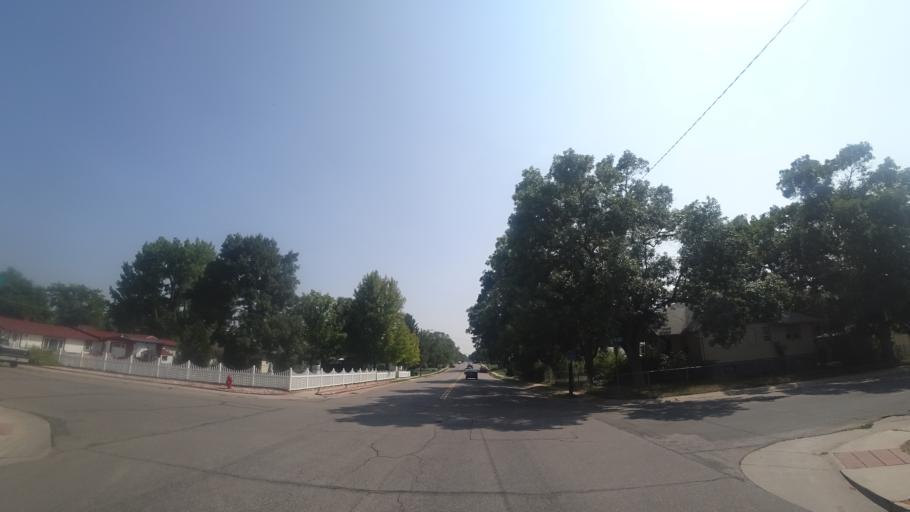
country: US
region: Colorado
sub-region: Arapahoe County
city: Englewood
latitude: 39.6315
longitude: -104.9832
